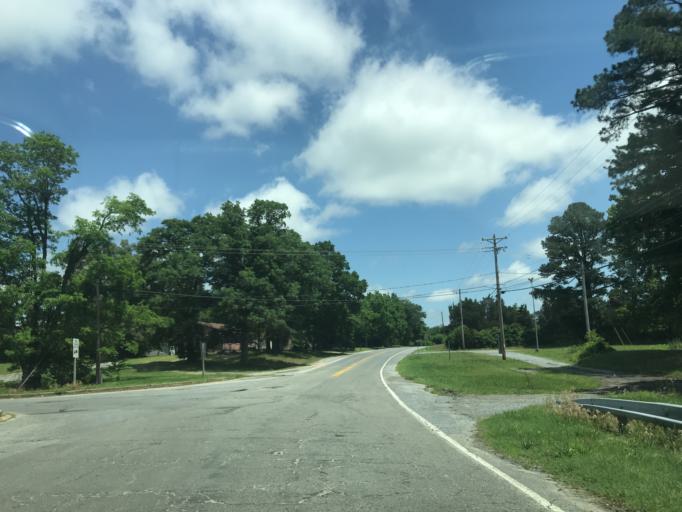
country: US
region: Maryland
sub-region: Caroline County
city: Federalsburg
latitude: 38.6963
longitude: -75.7647
